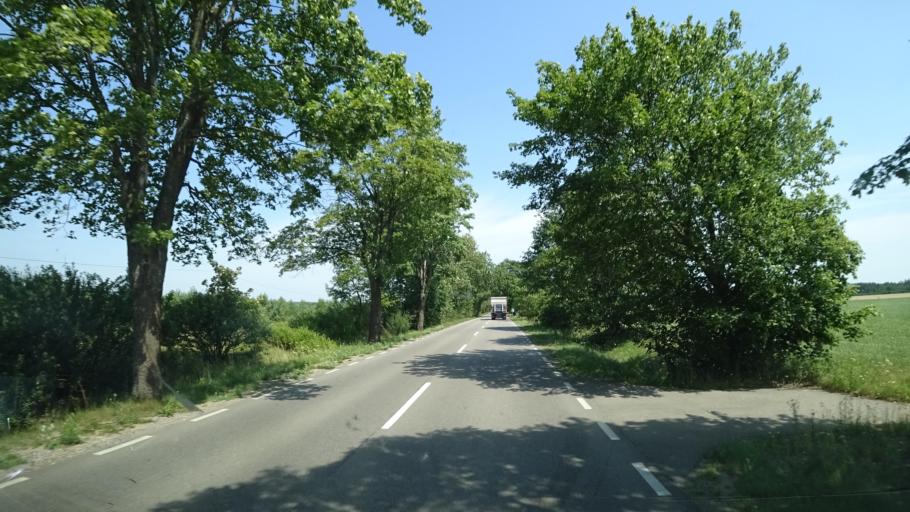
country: PL
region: Pomeranian Voivodeship
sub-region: Powiat koscierski
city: Lipusz
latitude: 54.1254
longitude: 17.8545
